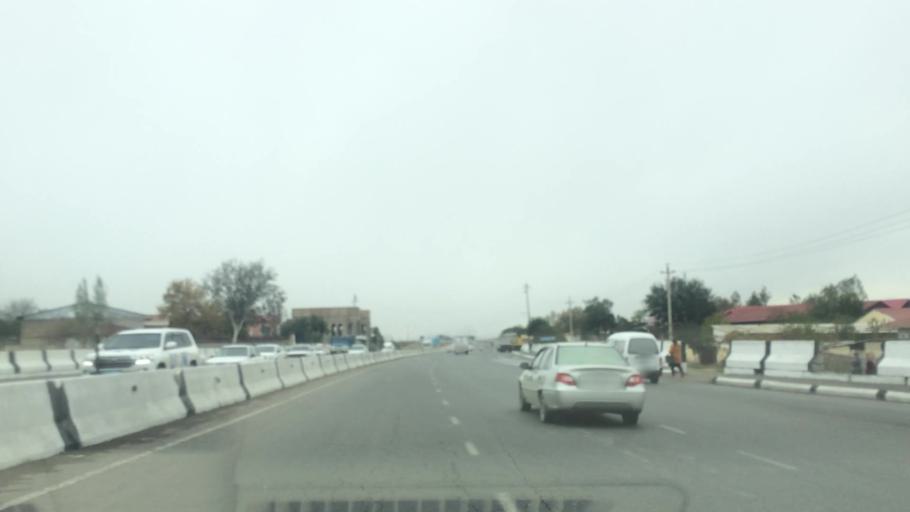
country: UZ
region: Samarqand
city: Jomboy
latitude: 39.6990
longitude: 67.0745
